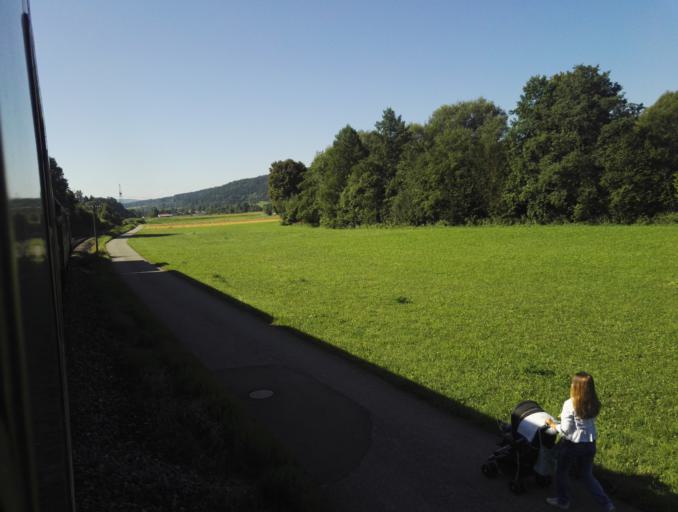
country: DE
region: Baden-Wuerttemberg
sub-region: Regierungsbezirk Stuttgart
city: Rudersberg
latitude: 48.8559
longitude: 9.5379
